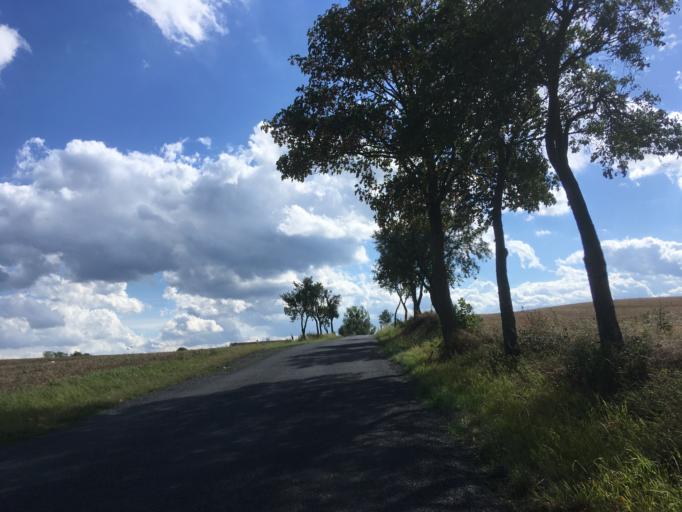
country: DE
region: Brandenburg
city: Angermunde
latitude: 52.9551
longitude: 14.0026
